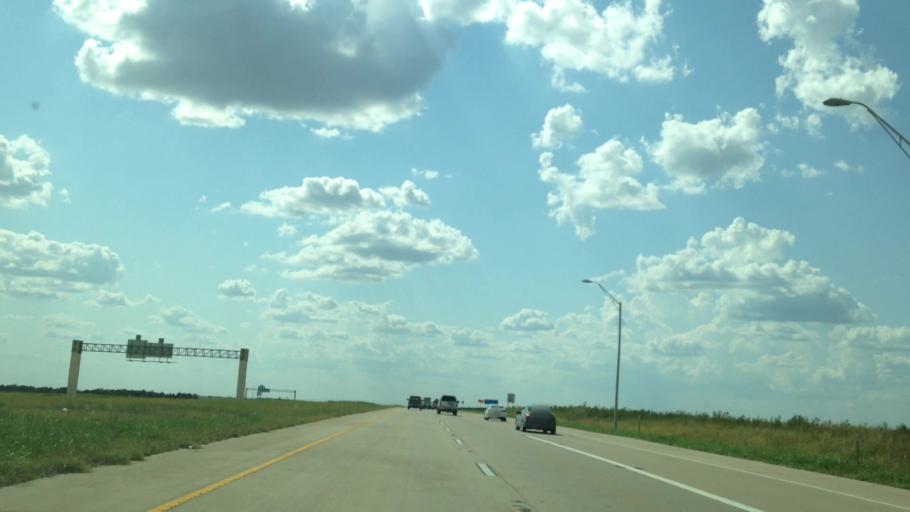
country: US
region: Texas
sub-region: Travis County
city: Onion Creek
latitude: 30.0816
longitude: -97.7049
